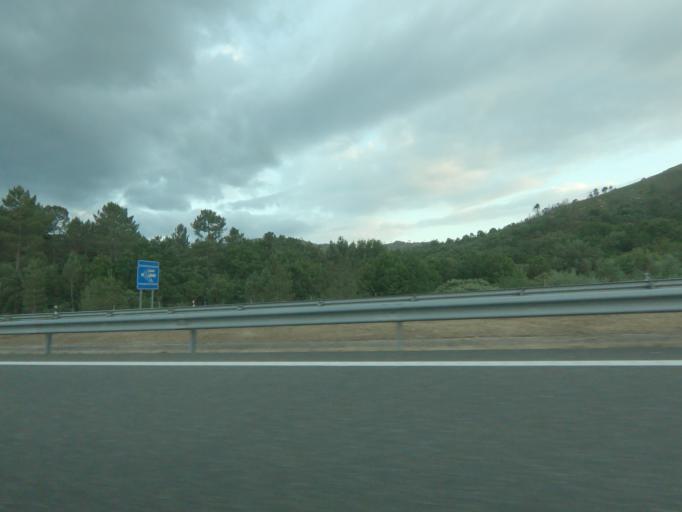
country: ES
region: Galicia
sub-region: Provincia de Ourense
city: Carballeda de Avia
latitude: 42.3100
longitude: -8.1667
